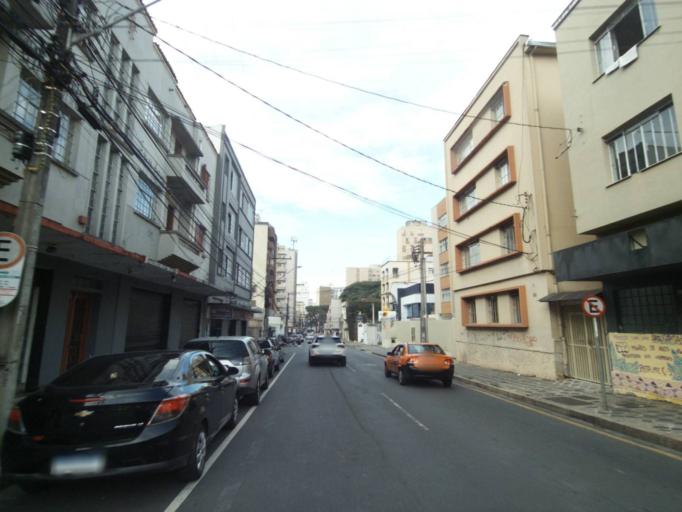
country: BR
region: Parana
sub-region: Curitiba
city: Curitiba
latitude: -25.4322
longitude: -49.2814
